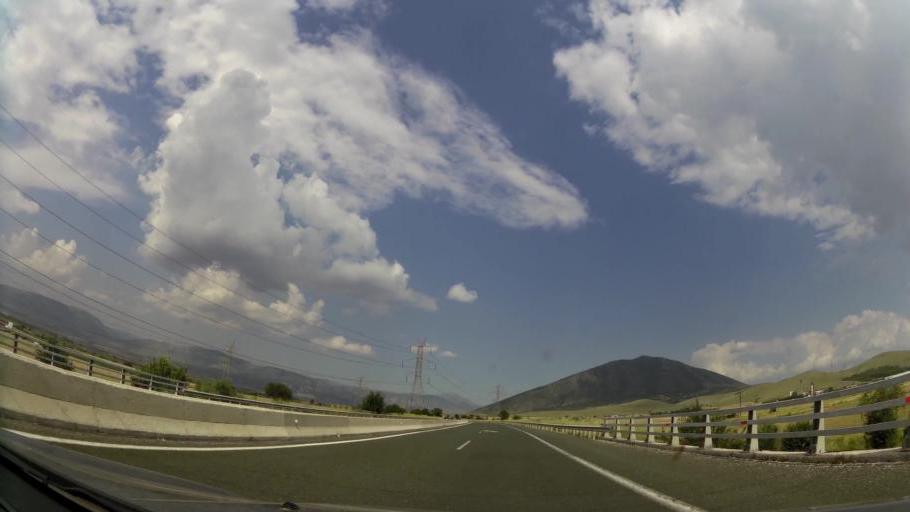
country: GR
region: West Macedonia
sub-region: Nomos Kozanis
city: Koila
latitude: 40.3610
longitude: 21.8480
